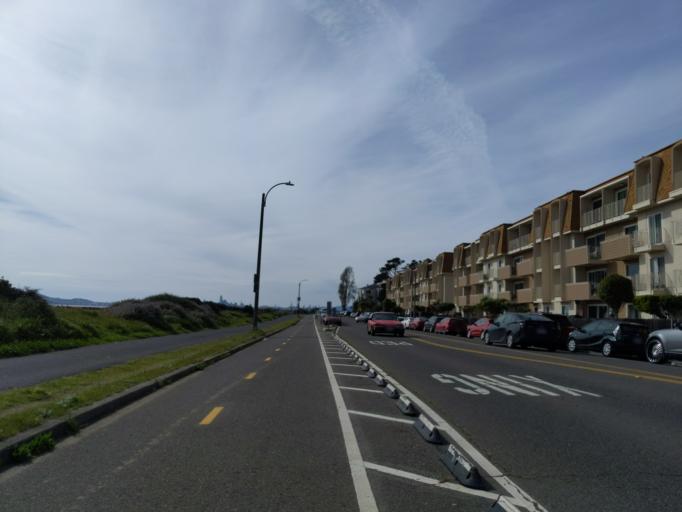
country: US
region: California
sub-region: Alameda County
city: Alameda
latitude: 37.7614
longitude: -122.2693
